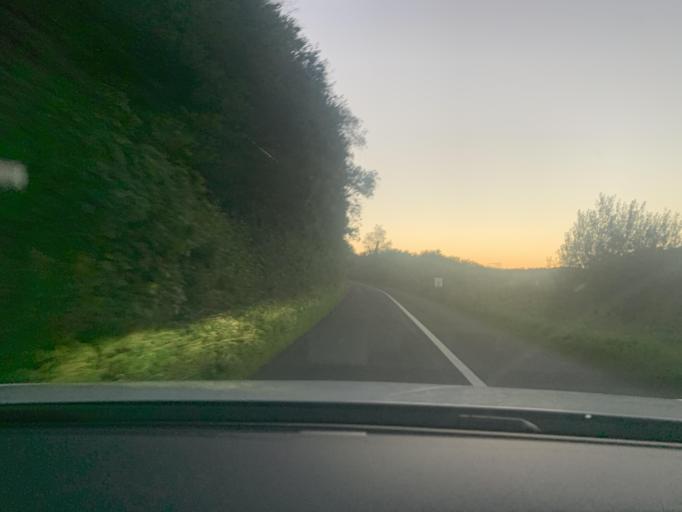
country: IE
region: Connaught
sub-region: County Leitrim
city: Manorhamilton
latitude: 54.2749
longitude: -8.3104
